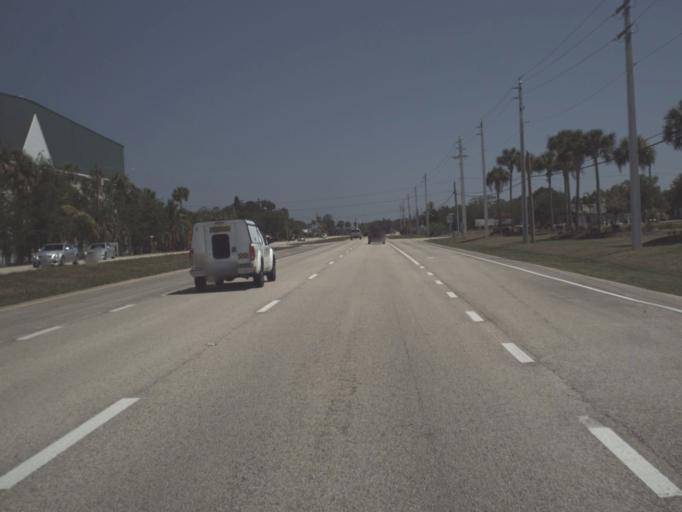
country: US
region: Florida
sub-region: Brevard County
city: Micco
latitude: 27.8704
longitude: -80.4962
